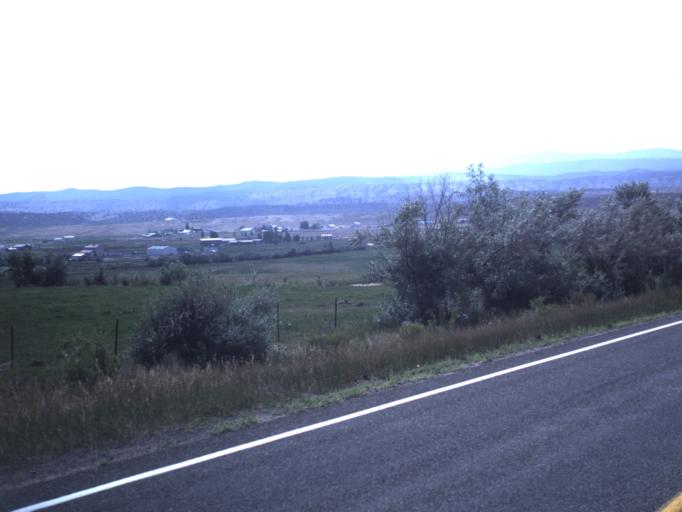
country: US
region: Utah
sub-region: Daggett County
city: Manila
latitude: 40.9822
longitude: -109.7227
